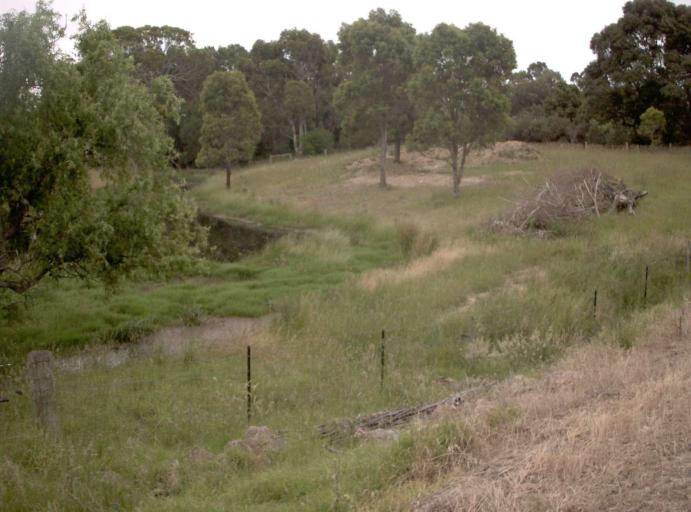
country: AU
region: Victoria
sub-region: East Gippsland
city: Bairnsdale
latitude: -37.8565
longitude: 147.5643
